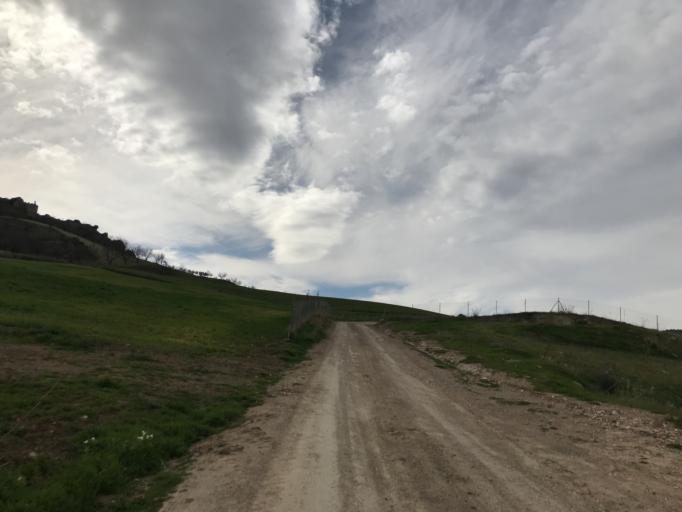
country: ES
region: Andalusia
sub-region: Provincia de Malaga
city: Ardales
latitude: 36.8746
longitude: -4.8790
